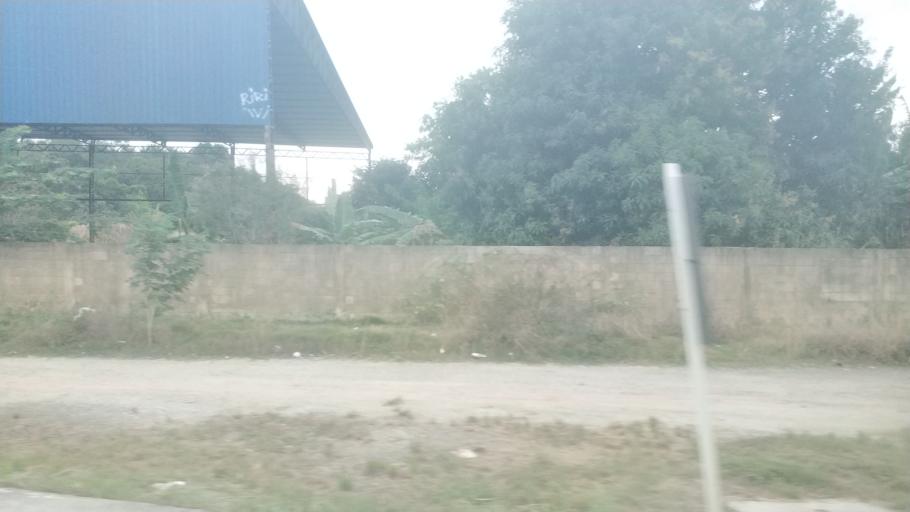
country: BR
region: Rio de Janeiro
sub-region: Seropedica
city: Seropedica
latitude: -22.7546
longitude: -43.6924
